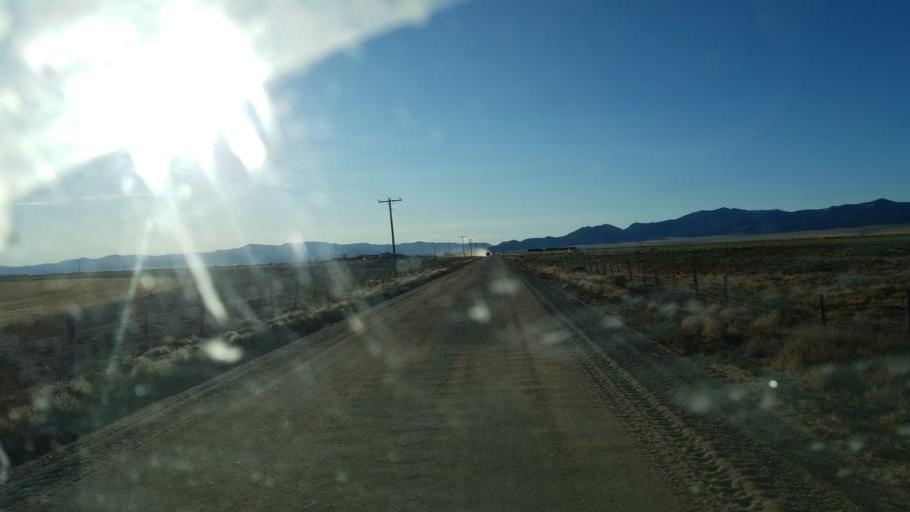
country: US
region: Colorado
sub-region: Saguache County
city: Saguache
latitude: 38.1004
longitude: -105.9081
